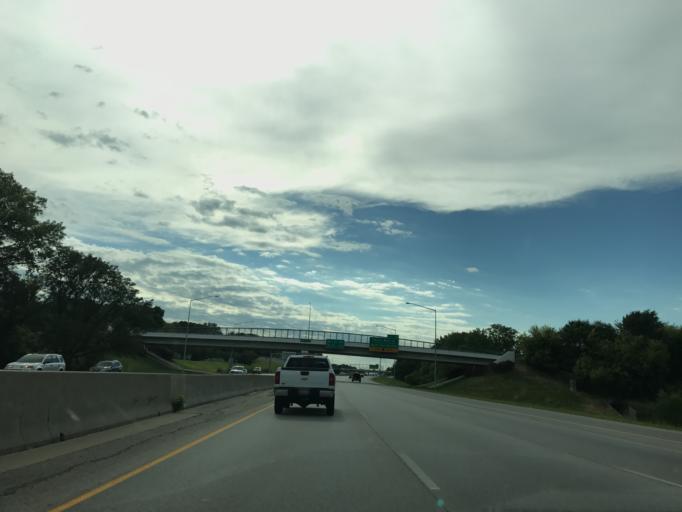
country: US
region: Iowa
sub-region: Polk County
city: Clive
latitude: 41.5925
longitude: -93.7400
